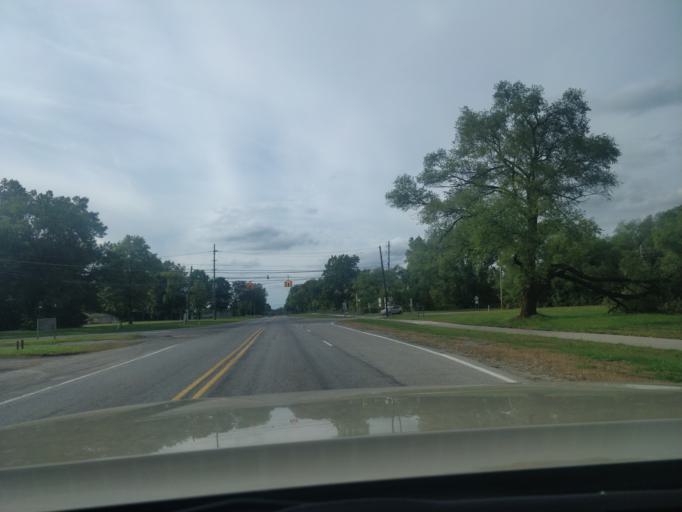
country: US
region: Michigan
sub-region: Wayne County
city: Romulus
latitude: 42.2109
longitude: -83.4039
